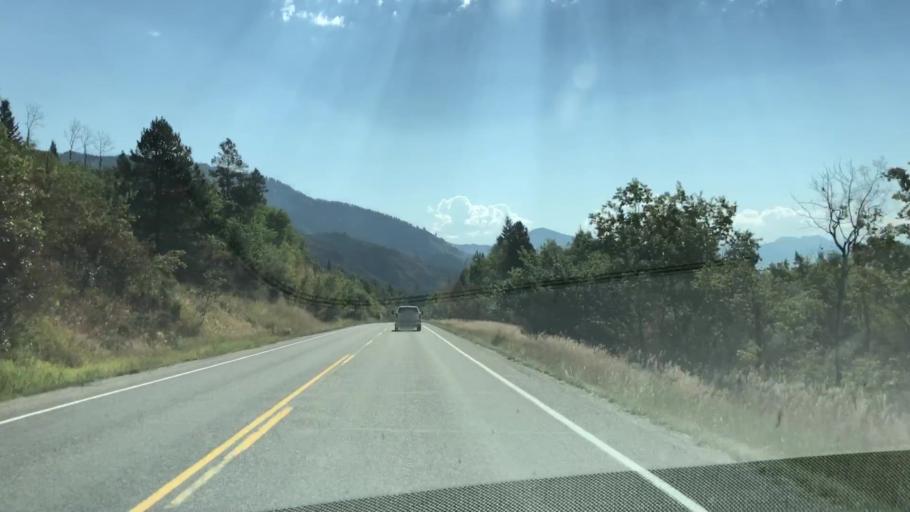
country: US
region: Wyoming
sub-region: Teton County
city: Hoback
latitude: 43.2268
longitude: -111.0838
